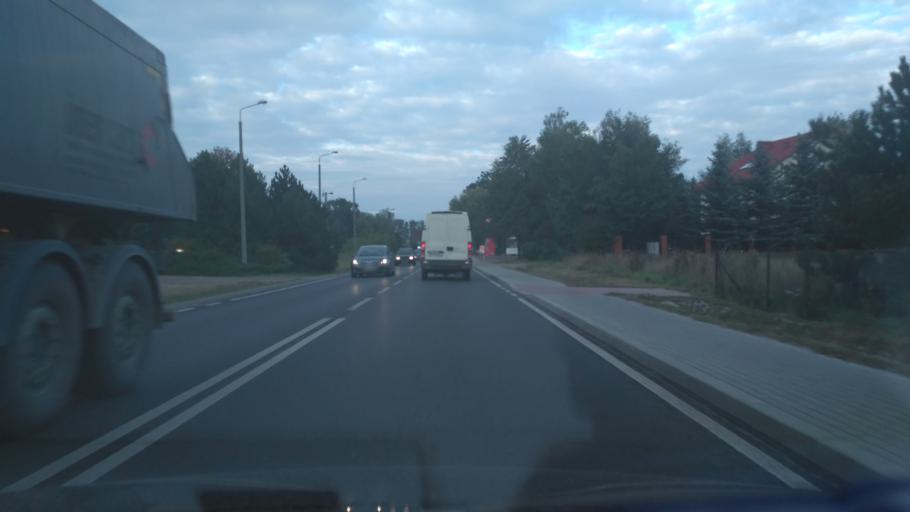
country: PL
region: Lublin Voivodeship
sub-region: Powiat leczynski
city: Spiczyn
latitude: 51.2995
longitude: 22.7221
